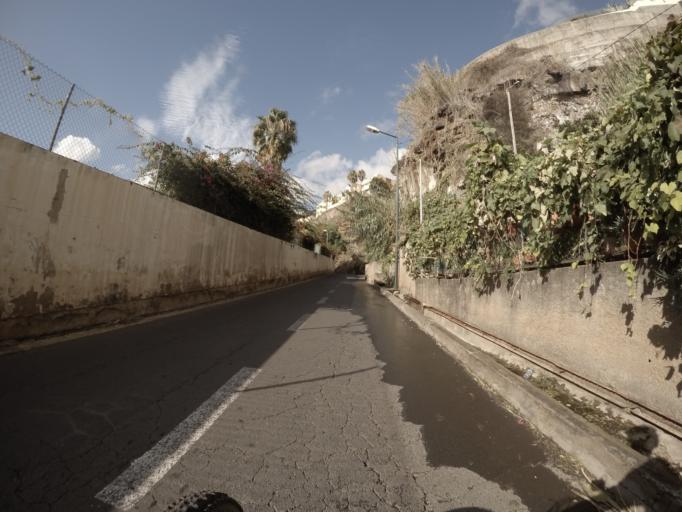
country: PT
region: Madeira
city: Camara de Lobos
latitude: 32.6404
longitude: -16.9507
